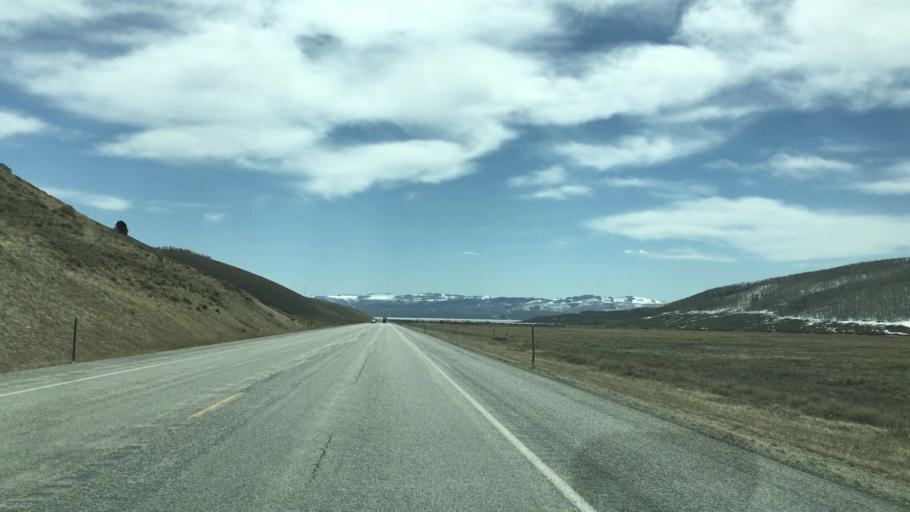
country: US
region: Utah
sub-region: Wasatch County
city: Heber
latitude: 40.2605
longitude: -111.2059
